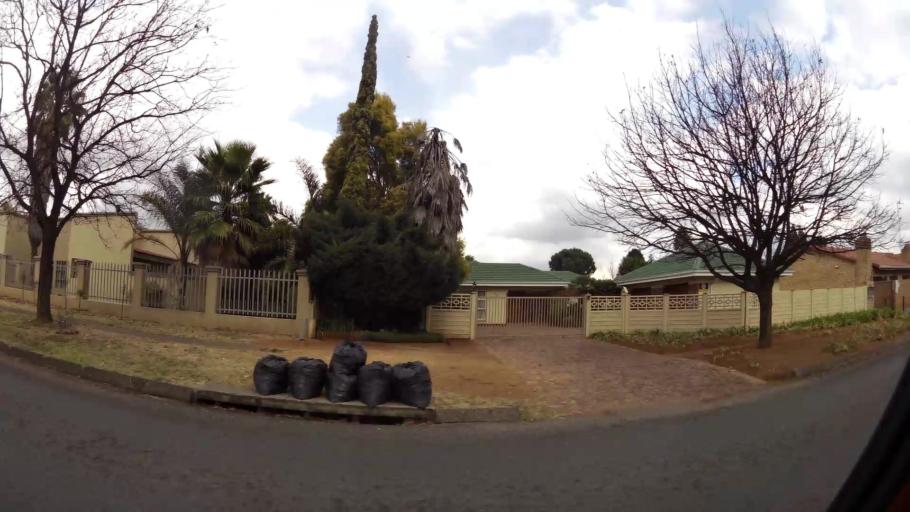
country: ZA
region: Gauteng
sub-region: Sedibeng District Municipality
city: Vanderbijlpark
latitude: -26.7316
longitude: 27.8486
